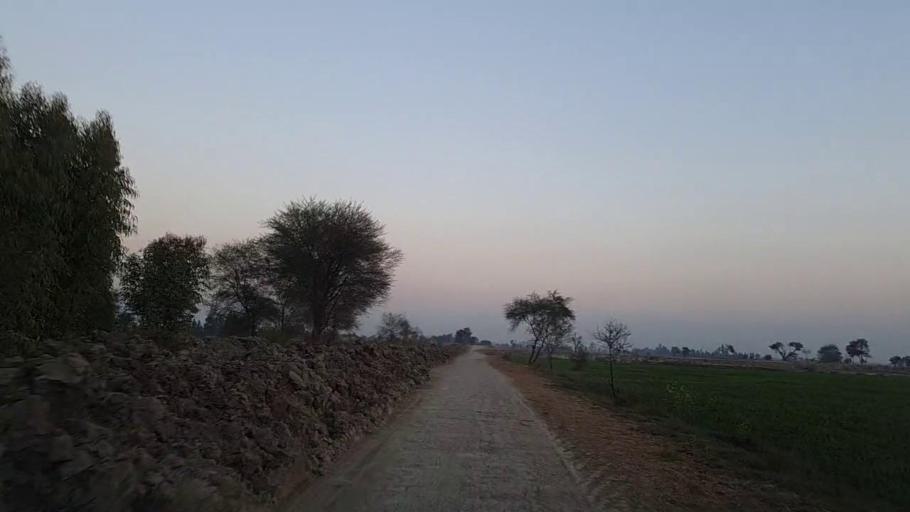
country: PK
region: Sindh
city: Naushahro Firoz
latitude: 26.7948
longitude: 68.0384
